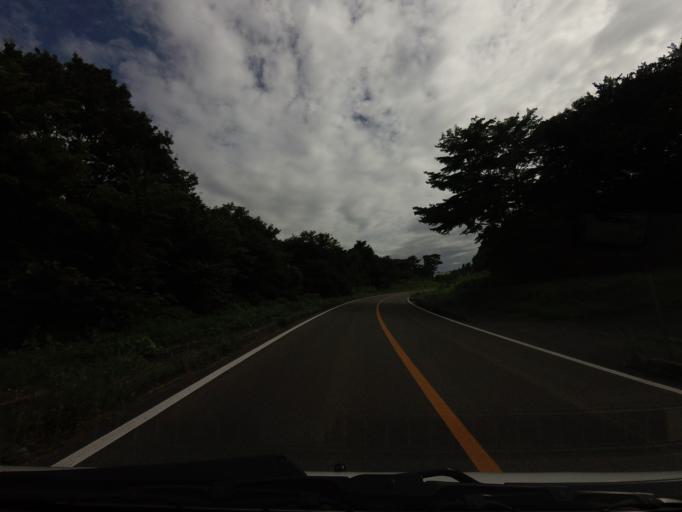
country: JP
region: Fukushima
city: Nihommatsu
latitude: 37.6090
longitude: 140.3595
